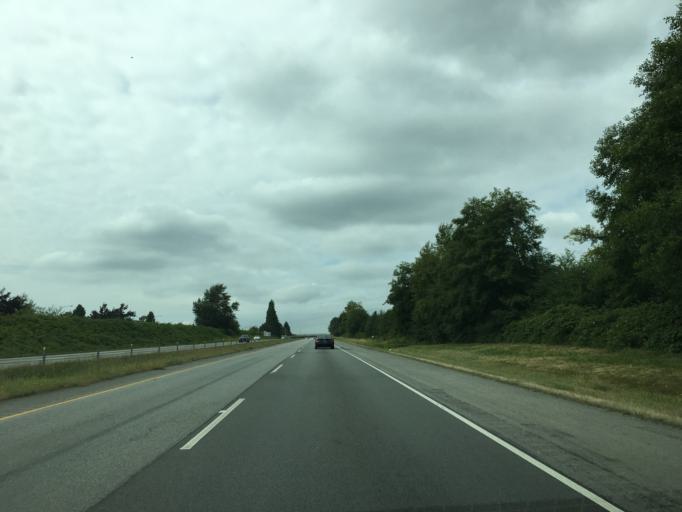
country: CA
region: British Columbia
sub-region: Greater Vancouver Regional District
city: White Rock
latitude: 49.0411
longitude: -122.7802
